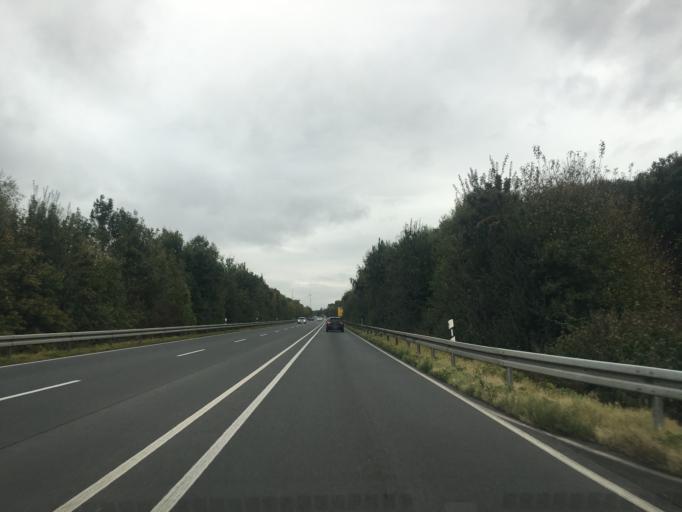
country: DE
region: North Rhine-Westphalia
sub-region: Regierungsbezirk Munster
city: Metelen
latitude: 52.1783
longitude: 7.2478
